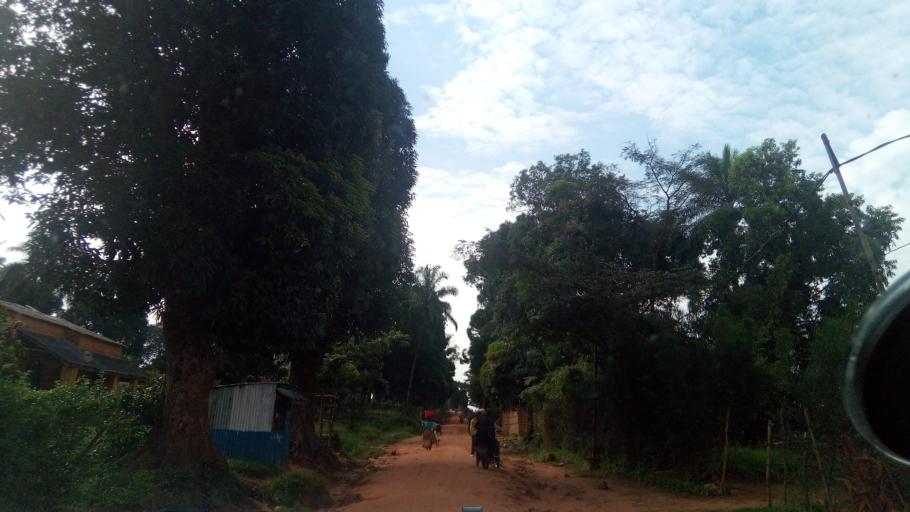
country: CD
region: Kasai-Oriental
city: Kabinda
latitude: -6.1313
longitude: 24.4846
